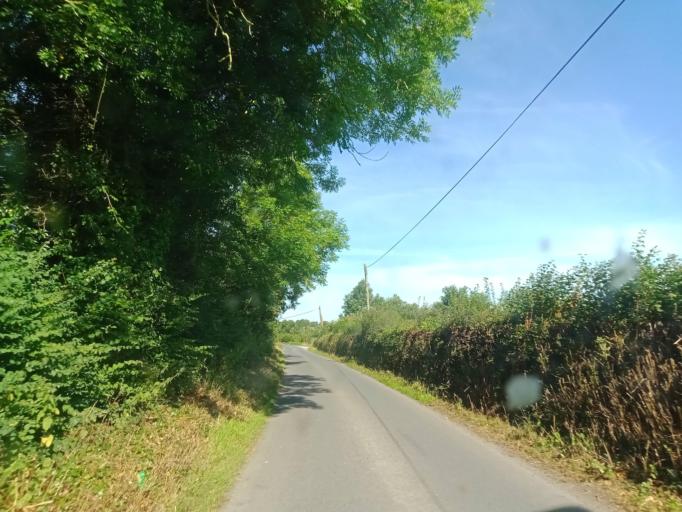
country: IE
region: Leinster
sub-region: Kilkenny
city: Ballyragget
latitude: 52.8083
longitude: -7.4309
